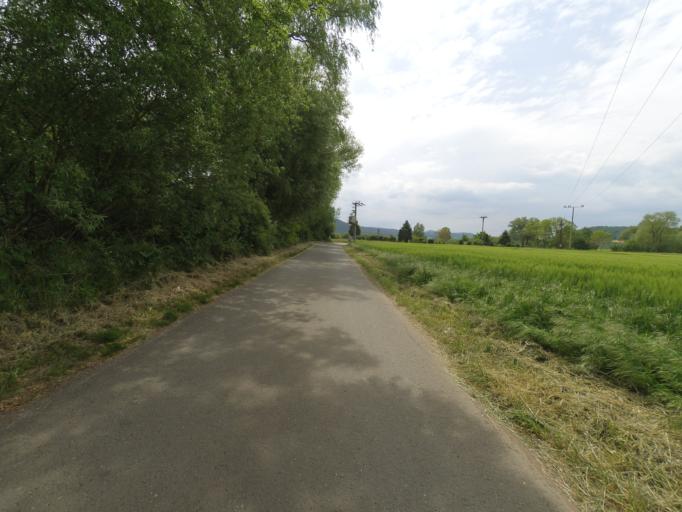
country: DE
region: Thuringia
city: Sulza
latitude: 50.8631
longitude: 11.6087
